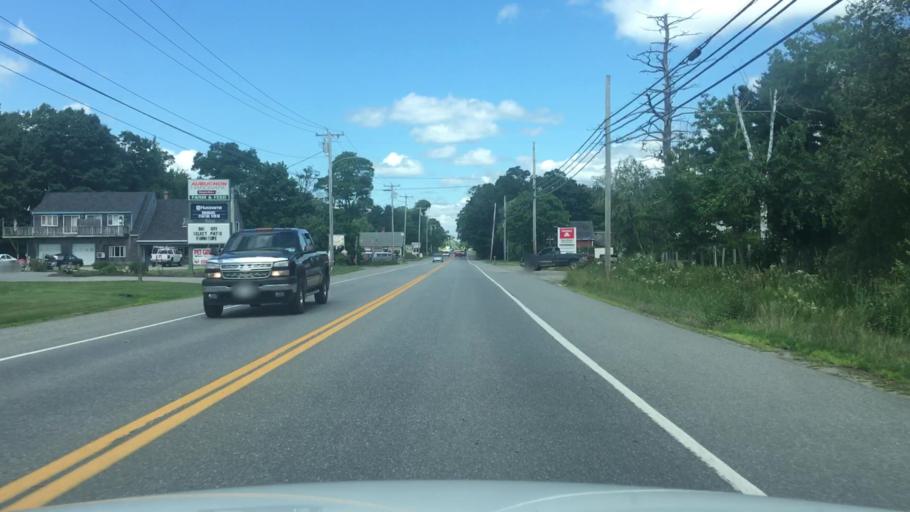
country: US
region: Maine
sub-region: Waldo County
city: Belfast
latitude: 44.4021
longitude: -68.9889
